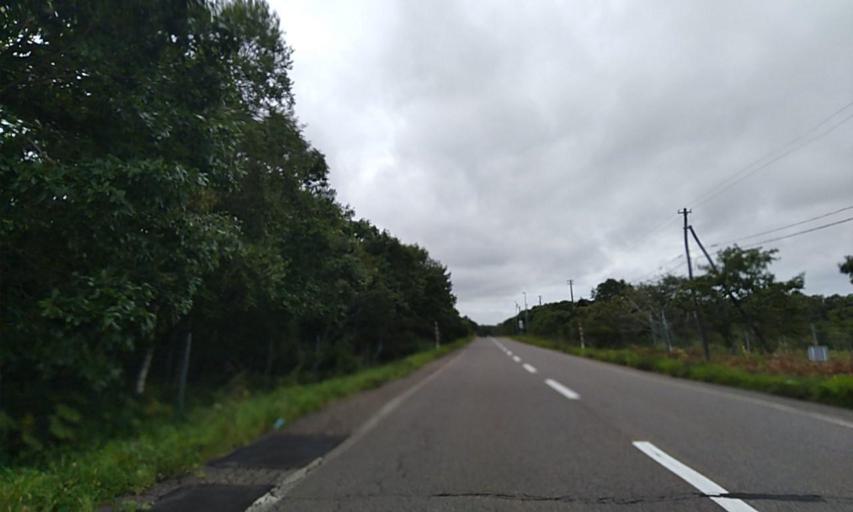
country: JP
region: Hokkaido
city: Nemuro
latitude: 43.3645
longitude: 145.2767
